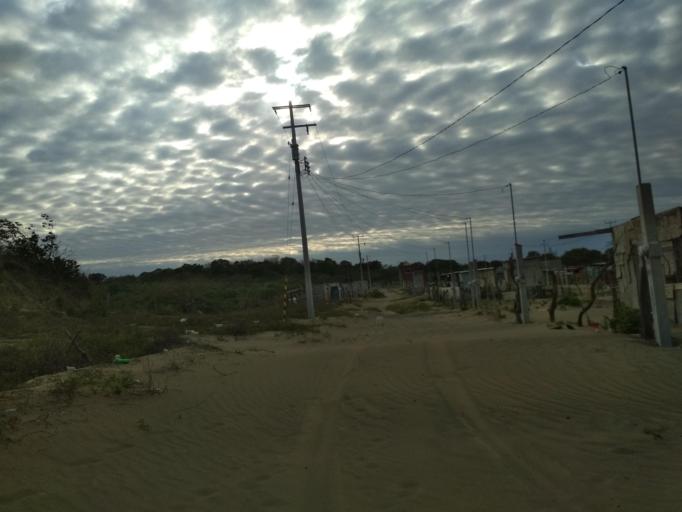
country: MX
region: Veracruz
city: Anton Lizardo
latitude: 19.0438
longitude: -95.9910
